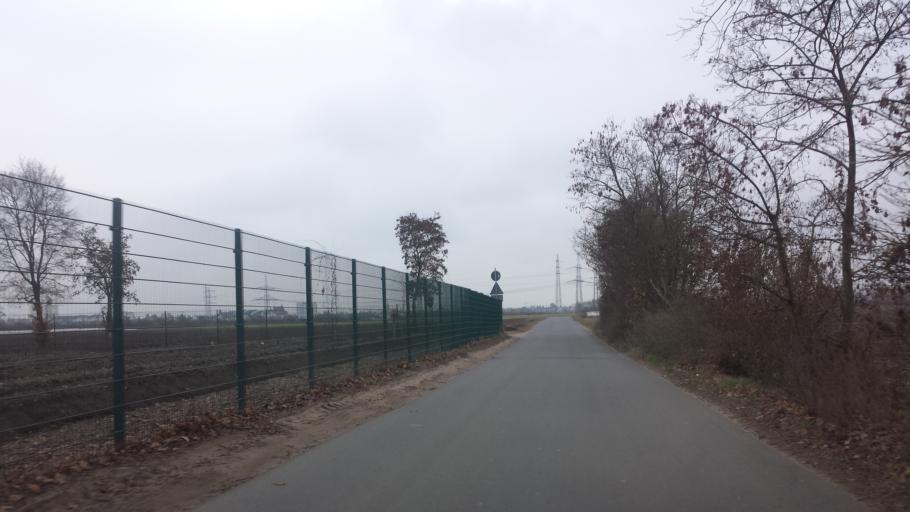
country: DE
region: Hesse
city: Lampertheim
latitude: 49.6166
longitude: 8.4768
